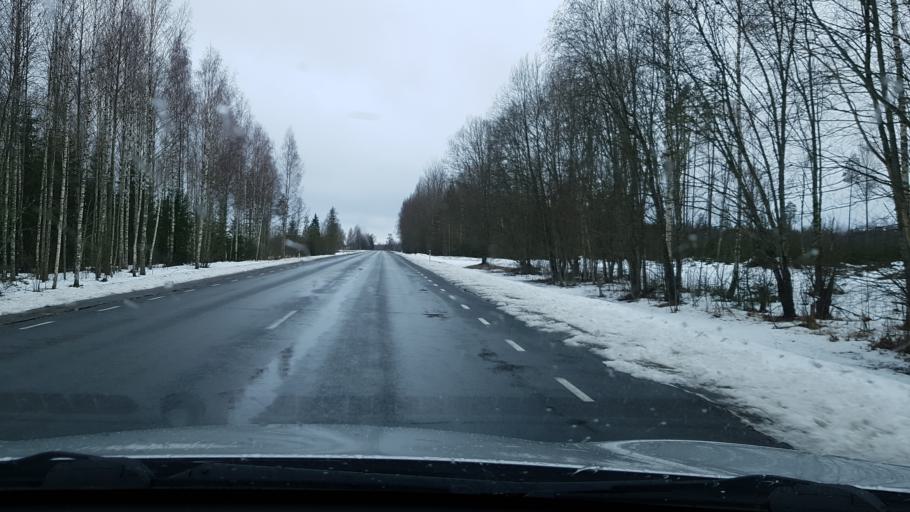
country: LV
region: Apes Novads
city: Ape
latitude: 57.7052
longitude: 26.7482
